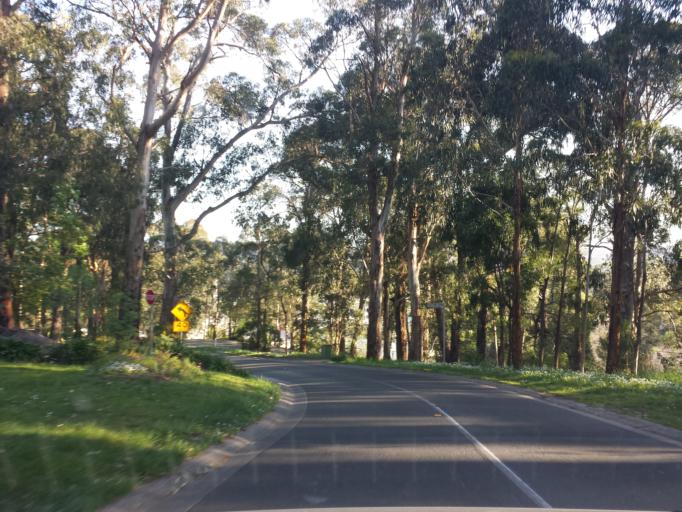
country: AU
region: Victoria
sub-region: Yarra Ranges
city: Belgrave
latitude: -37.9067
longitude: 145.3531
